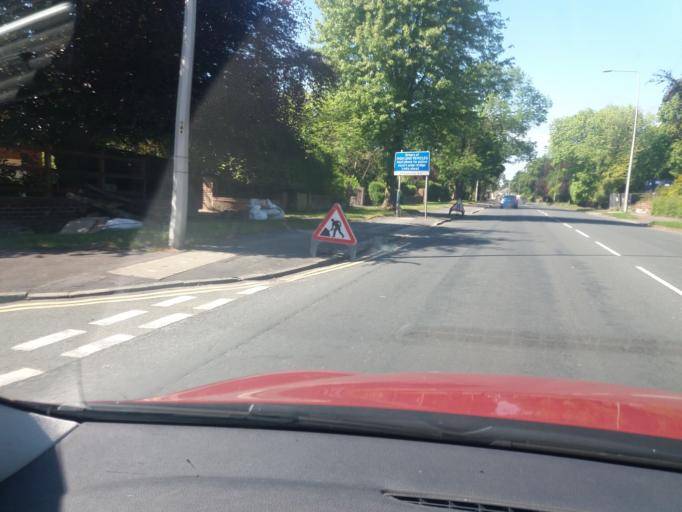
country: GB
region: England
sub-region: Lancashire
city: Preston
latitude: 53.7942
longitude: -2.7141
